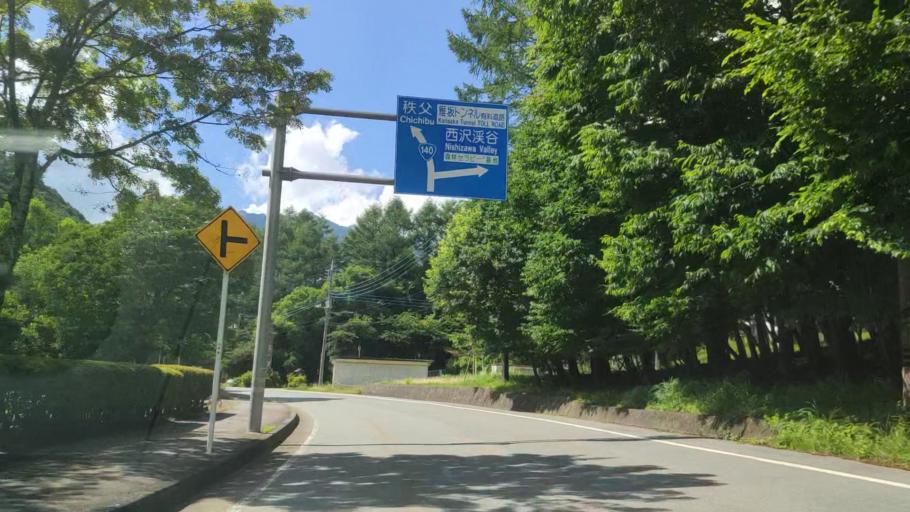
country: JP
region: Yamanashi
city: Enzan
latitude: 35.8614
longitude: 138.7566
